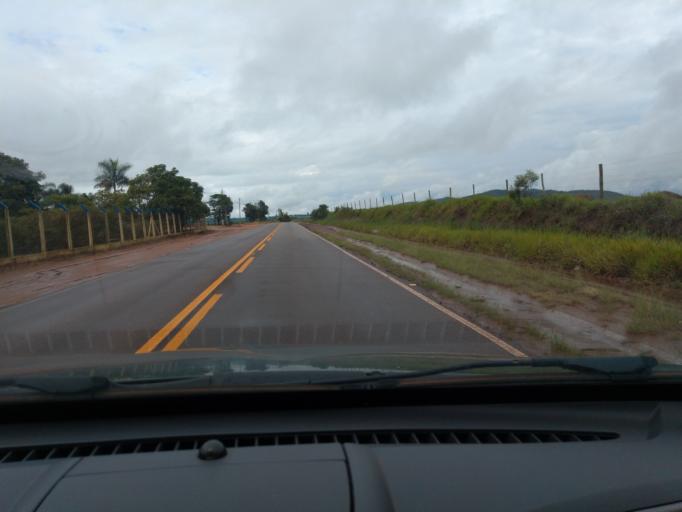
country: BR
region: Minas Gerais
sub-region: Tres Coracoes
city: Tres Coracoes
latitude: -21.6476
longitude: -45.1797
